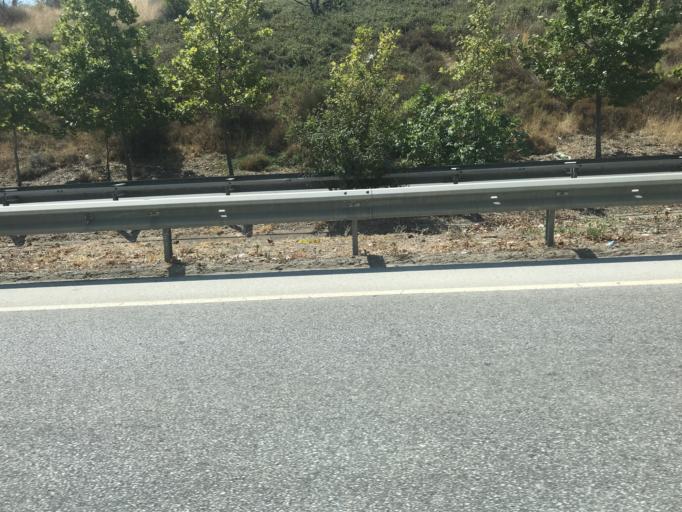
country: TR
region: Izmir
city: Urla
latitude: 38.3265
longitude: 26.7780
